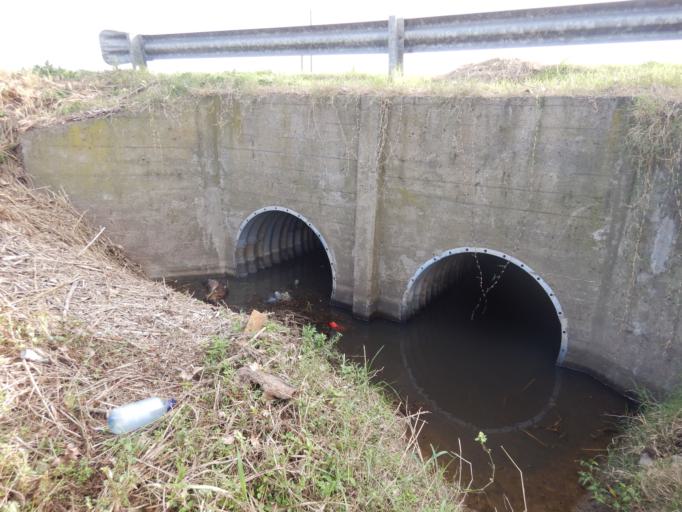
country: AR
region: Santa Fe
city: Roldan
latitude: -32.8963
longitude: -60.9606
